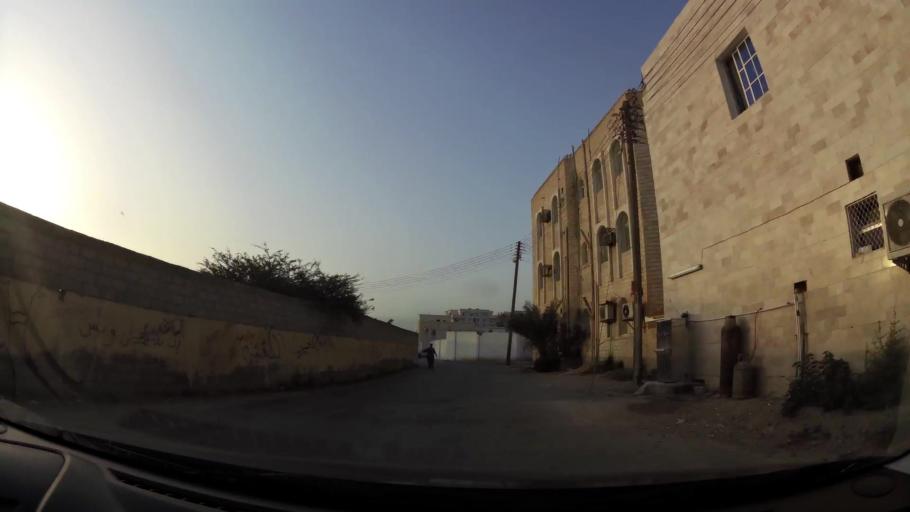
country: OM
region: Zufar
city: Salalah
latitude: 17.0171
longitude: 54.1144
